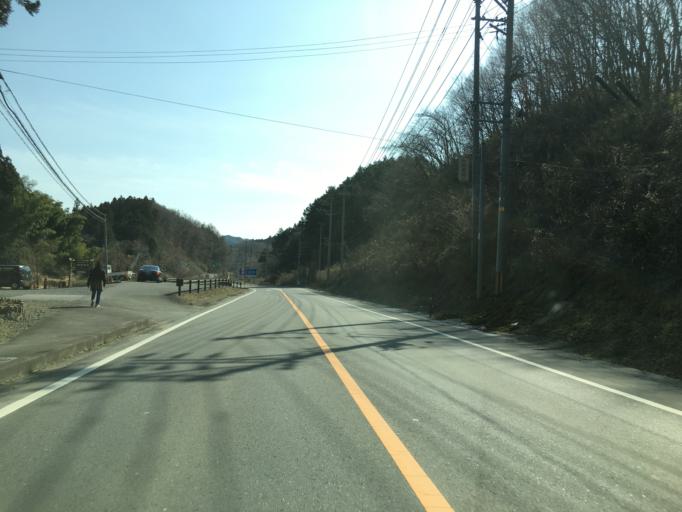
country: JP
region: Ibaraki
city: Daigo
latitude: 36.8556
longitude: 140.4298
